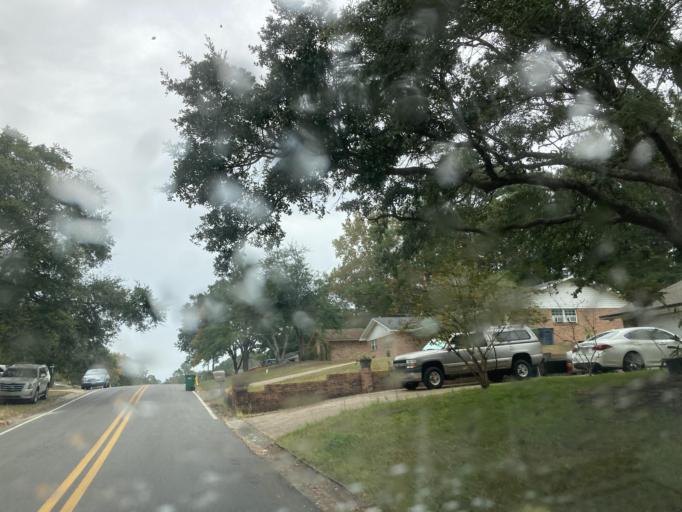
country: US
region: Mississippi
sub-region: Jackson County
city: Ocean Springs
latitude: 30.4295
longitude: -88.8162
